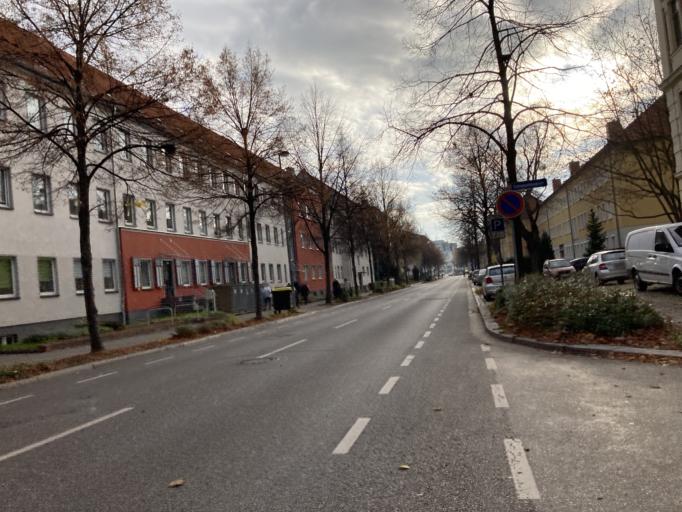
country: DE
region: Saxony-Anhalt
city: Magdeburg
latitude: 52.1375
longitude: 11.6152
